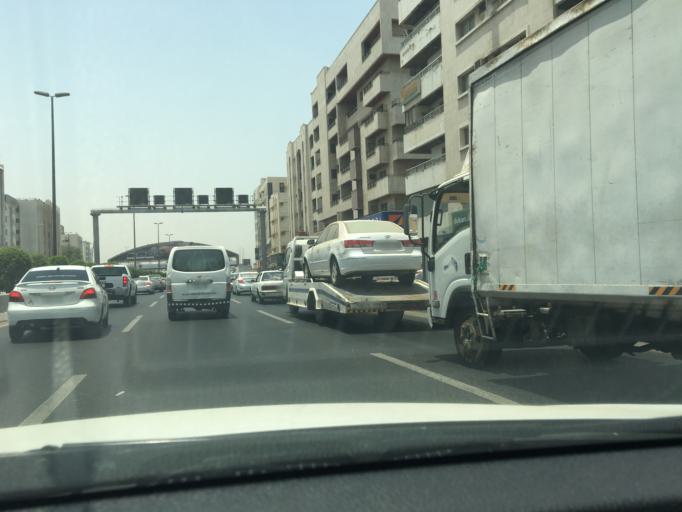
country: SA
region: Makkah
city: Jeddah
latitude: 21.5371
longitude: 39.1920
